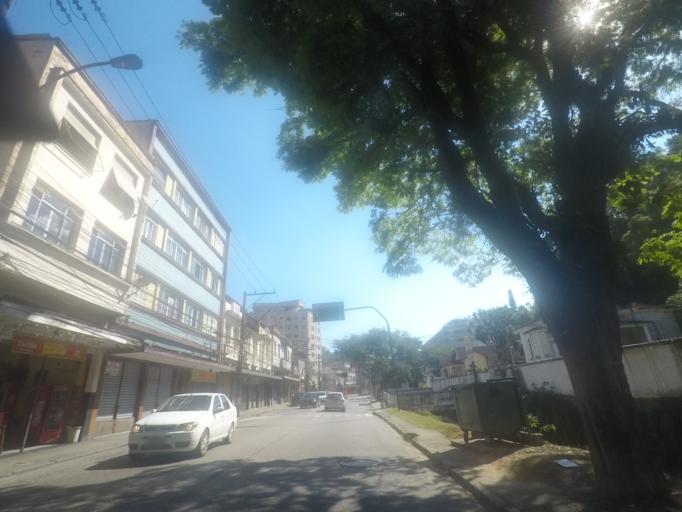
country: BR
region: Rio de Janeiro
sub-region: Petropolis
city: Petropolis
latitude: -22.5200
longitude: -43.1879
